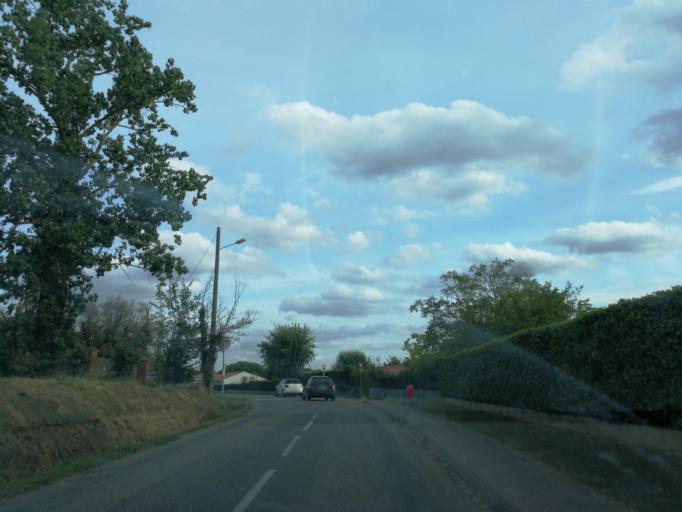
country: FR
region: Midi-Pyrenees
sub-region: Departement de la Haute-Garonne
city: Flourens
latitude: 43.5934
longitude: 1.5730
